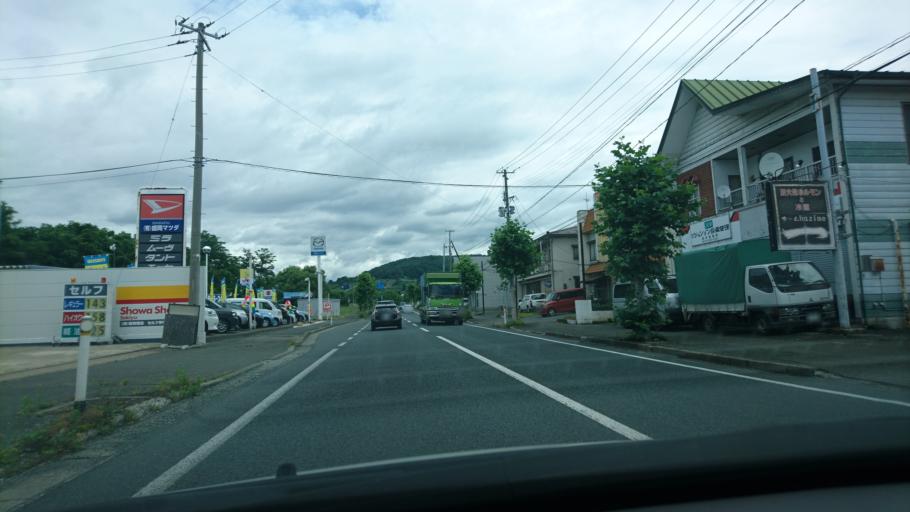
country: JP
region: Iwate
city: Morioka-shi
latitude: 39.6512
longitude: 141.1830
